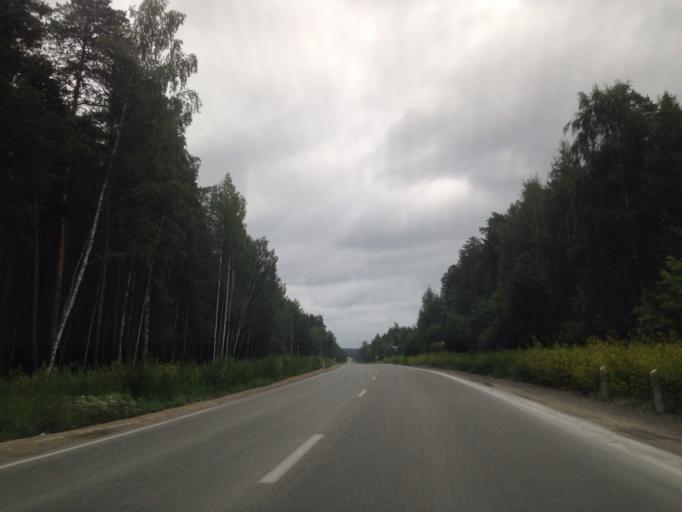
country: RU
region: Sverdlovsk
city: Istok
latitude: 56.8446
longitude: 60.7260
